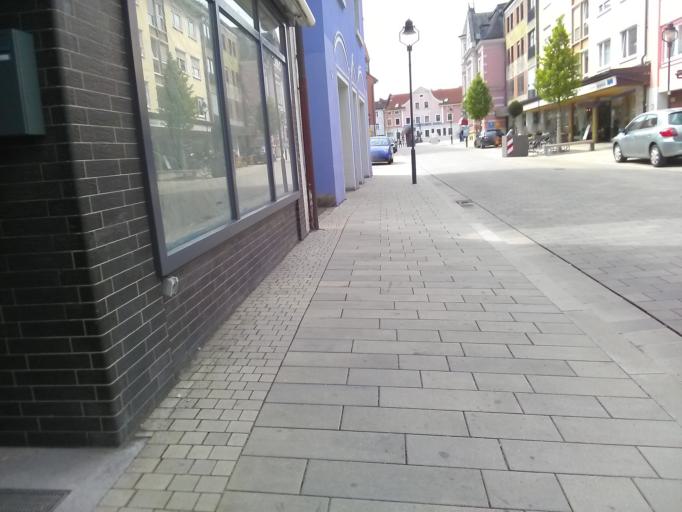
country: DE
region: Bavaria
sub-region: Regierungsbezirk Mittelfranken
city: Treuchtlingen
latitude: 48.9564
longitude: 10.9088
